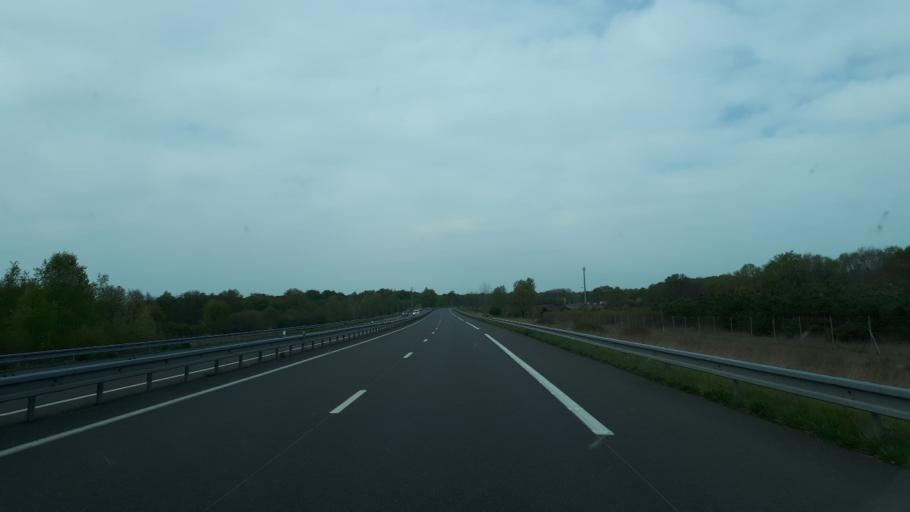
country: FR
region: Centre
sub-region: Departement du Loir-et-Cher
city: Selles-sur-Cher
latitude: 47.3377
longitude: 1.5946
